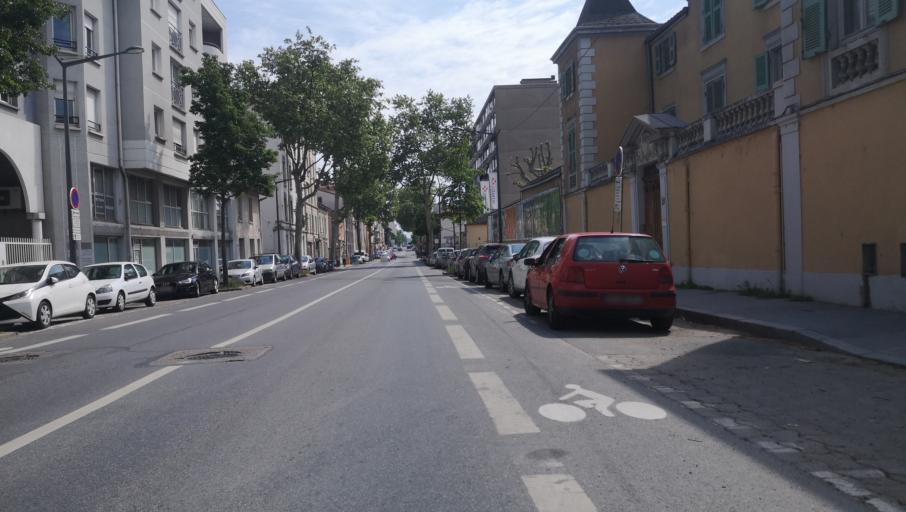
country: FR
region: Rhone-Alpes
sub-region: Departement du Rhone
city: Lyon
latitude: 45.7334
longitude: 4.8534
